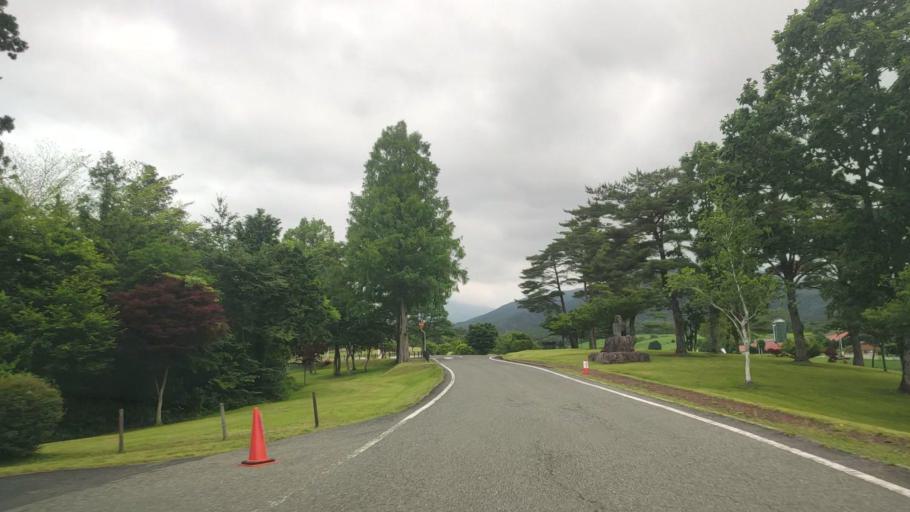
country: JP
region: Tottori
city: Kurayoshi
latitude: 35.2958
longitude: 133.6303
